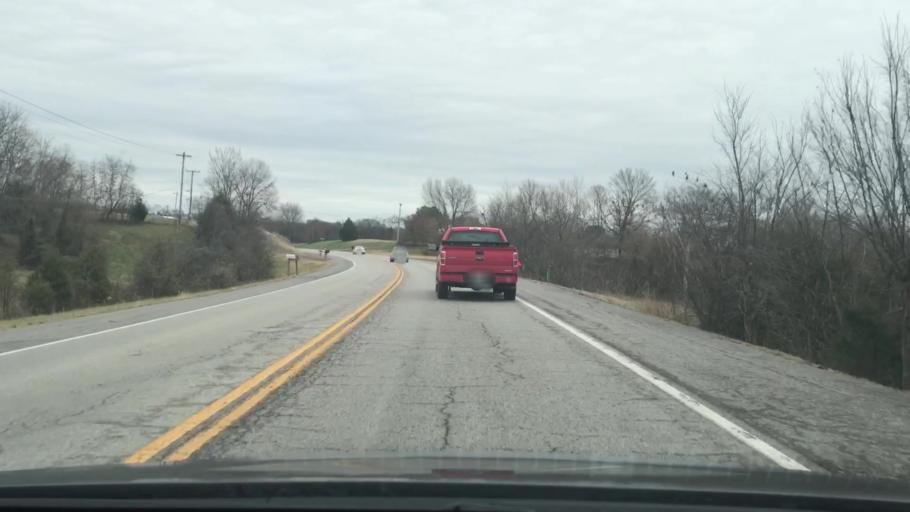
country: US
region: Tennessee
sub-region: Trousdale County
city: Hartsville
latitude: 36.3854
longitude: -86.2775
